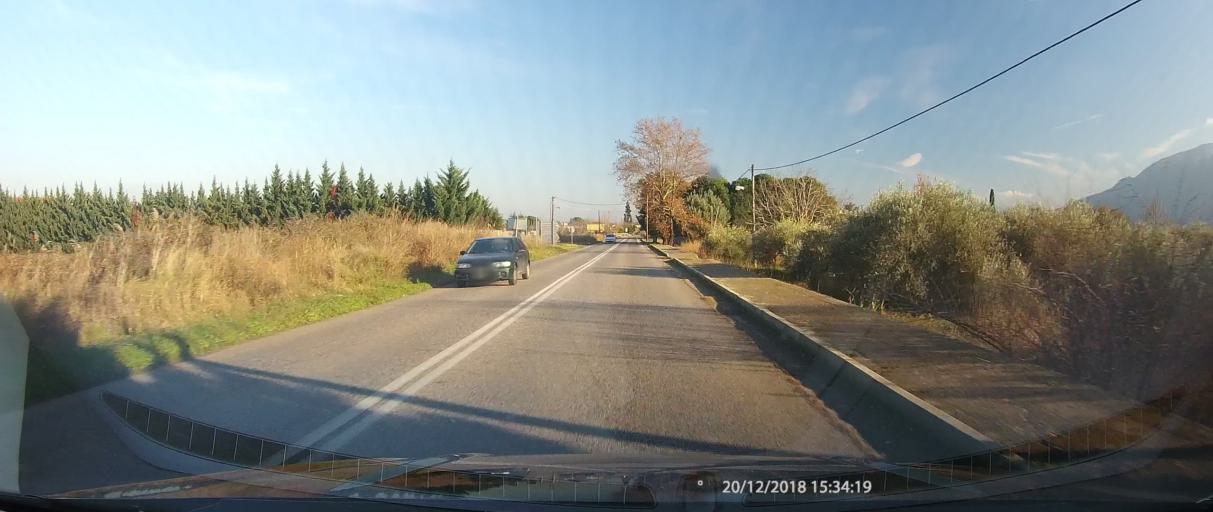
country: GR
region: Central Greece
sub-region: Nomos Fthiotidos
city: Lianokladhion
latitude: 38.9193
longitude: 22.2930
